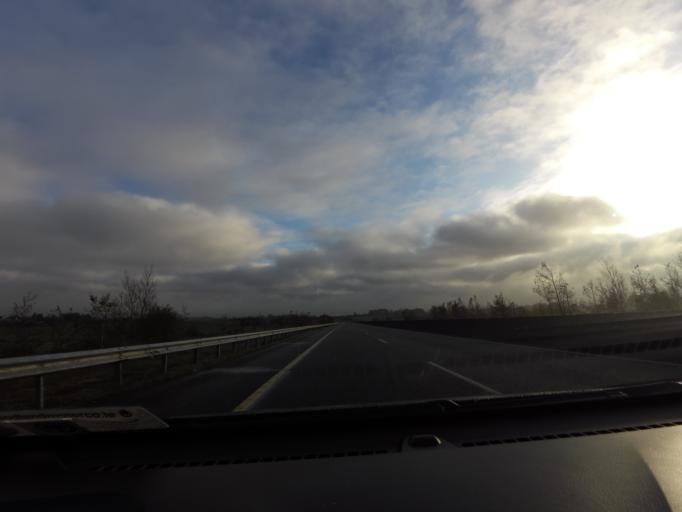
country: IE
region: Connaught
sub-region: County Galway
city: Loughrea
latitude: 53.2837
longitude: -8.4998
